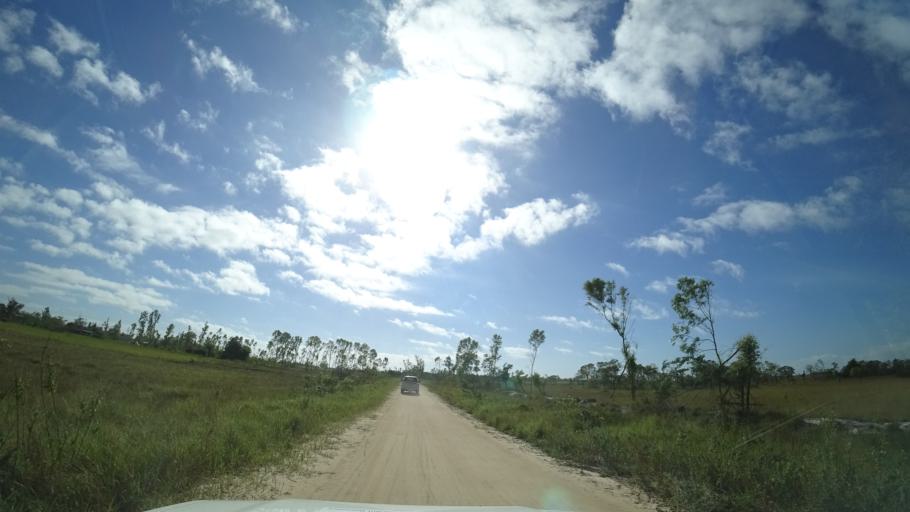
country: MZ
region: Sofala
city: Beira
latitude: -19.7217
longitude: 34.9978
